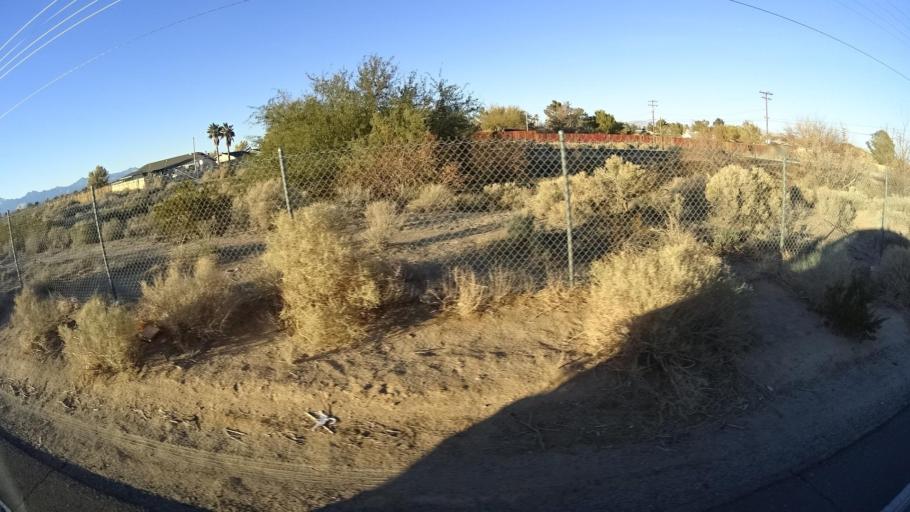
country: US
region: California
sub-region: Kern County
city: Ridgecrest
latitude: 35.6078
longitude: -117.6809
